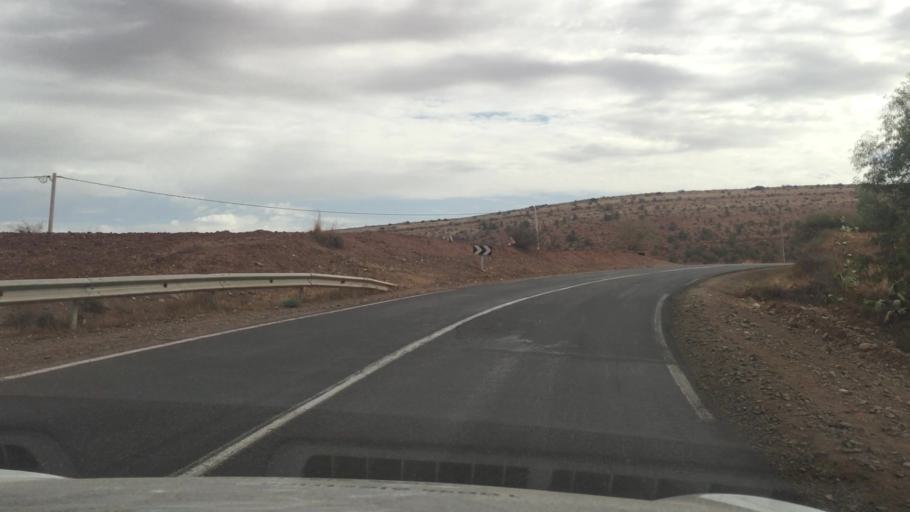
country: MA
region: Marrakech-Tensift-Al Haouz
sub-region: Al-Haouz
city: Touama
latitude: 31.5478
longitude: -7.5644
